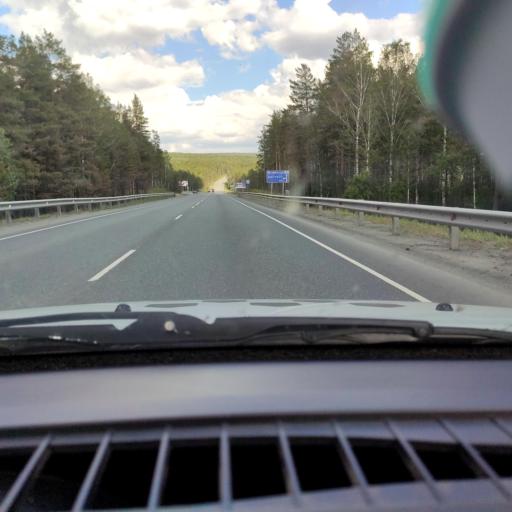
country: RU
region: Chelyabinsk
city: Zlatoust
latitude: 55.0558
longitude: 59.6906
